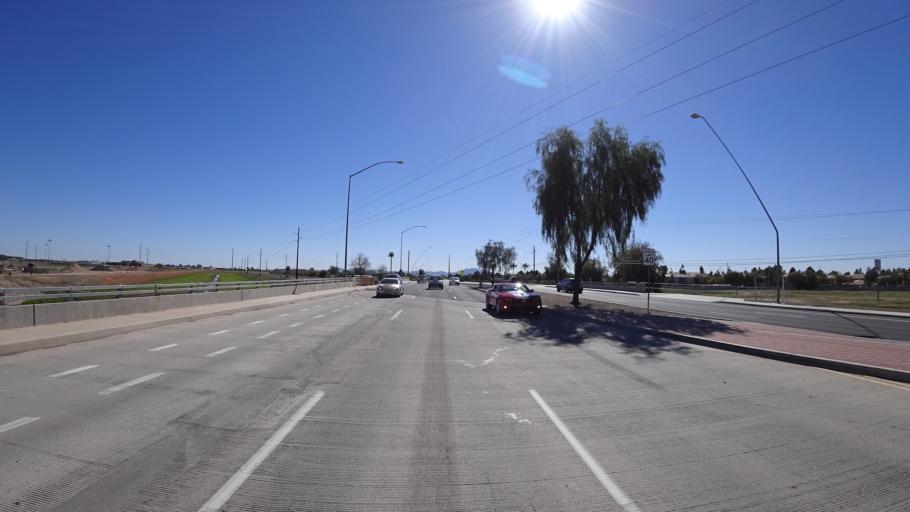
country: US
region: Arizona
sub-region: Maricopa County
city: Gilbert
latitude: 33.3639
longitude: -111.6876
